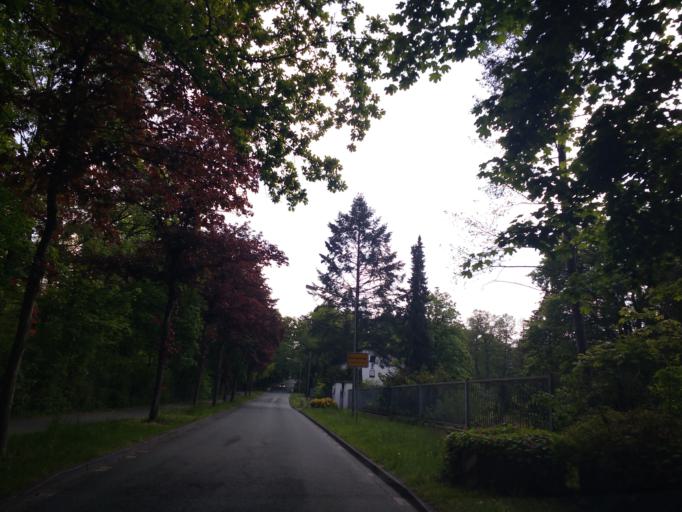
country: DE
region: North Rhine-Westphalia
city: Bad Lippspringe
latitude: 51.7880
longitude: 8.7998
